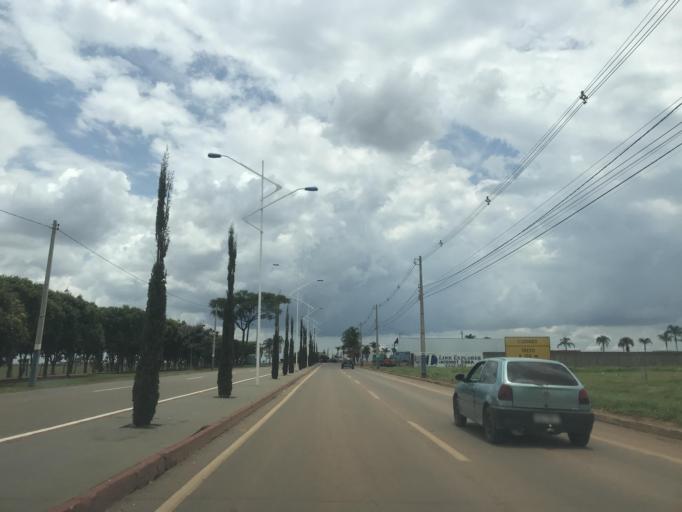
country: BR
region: Goias
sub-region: Vianopolis
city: Vianopolis
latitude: -16.7600
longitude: -48.5208
